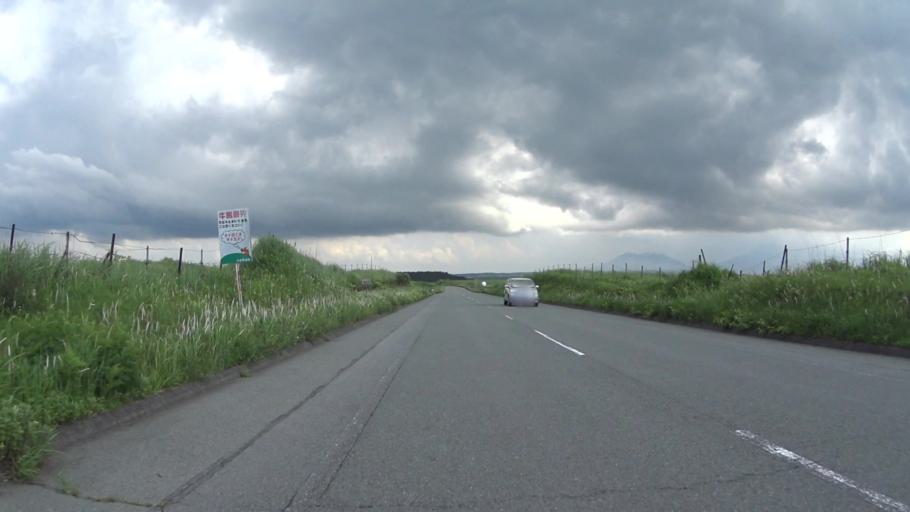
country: JP
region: Kumamoto
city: Aso
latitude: 33.0217
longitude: 131.1512
